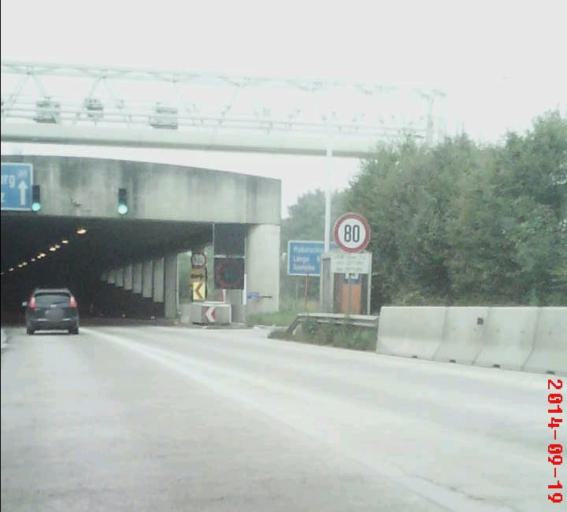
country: AT
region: Styria
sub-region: Graz Stadt
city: Wetzelsdorf
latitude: 47.0333
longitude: 15.4090
